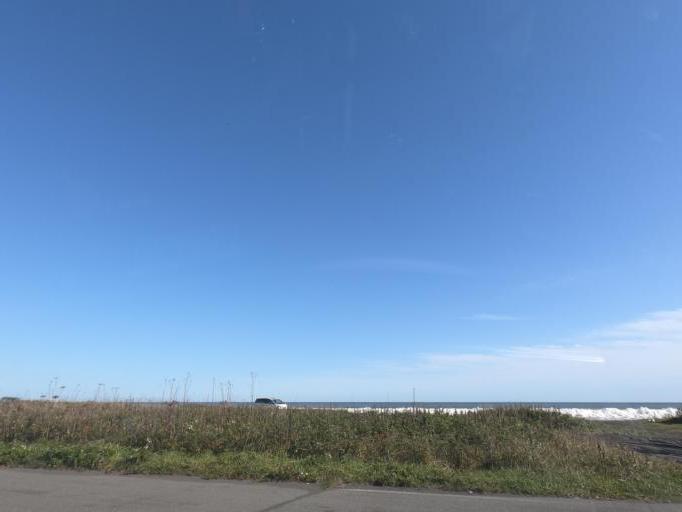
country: JP
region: Hokkaido
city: Obihiro
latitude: 42.5805
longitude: 143.5300
